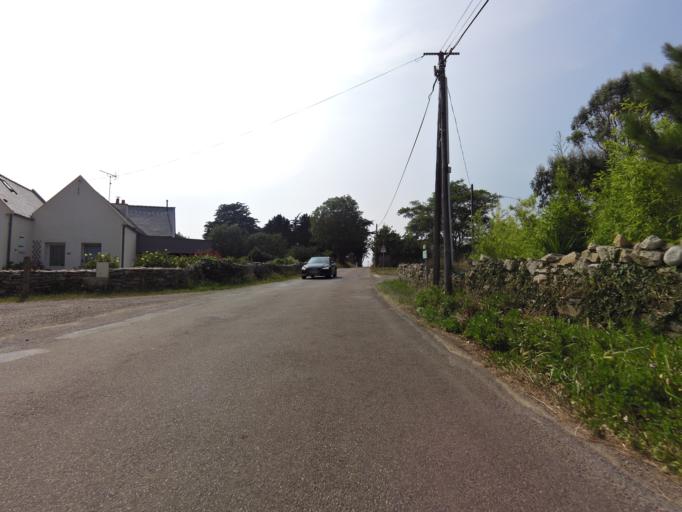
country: FR
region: Brittany
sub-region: Departement du Finistere
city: Esquibien
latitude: 48.0176
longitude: -4.5858
